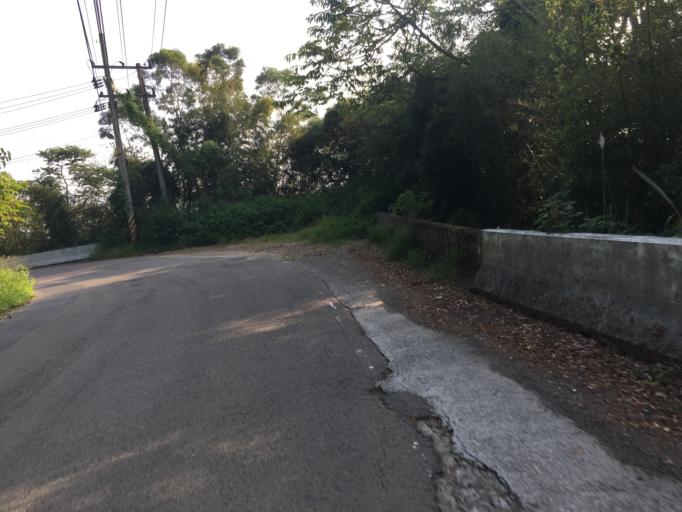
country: TW
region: Taiwan
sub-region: Hsinchu
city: Hsinchu
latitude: 24.7420
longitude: 121.0389
